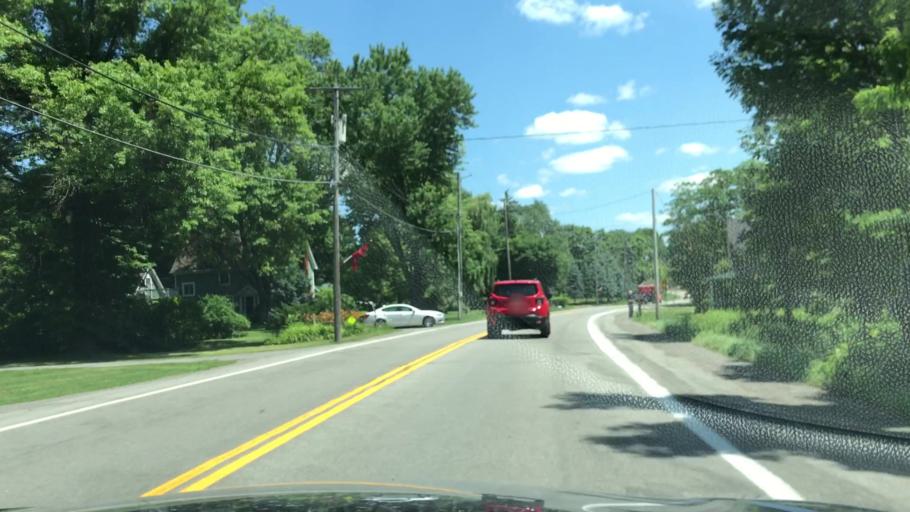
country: US
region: New York
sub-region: Erie County
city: East Aurora
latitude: 42.7676
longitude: -78.5811
